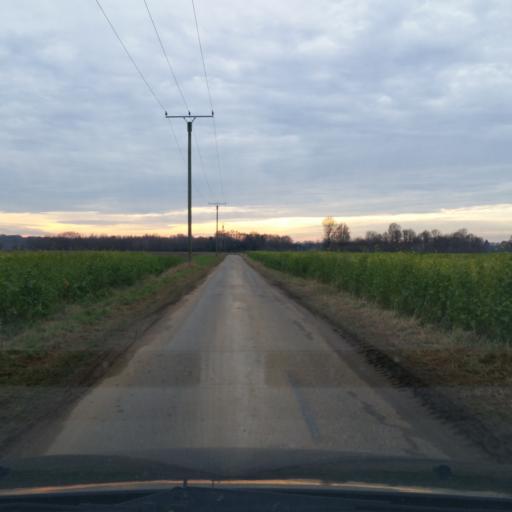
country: DE
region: North Rhine-Westphalia
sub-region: Regierungsbezirk Munster
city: Isselburg
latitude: 51.8162
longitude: 6.5123
